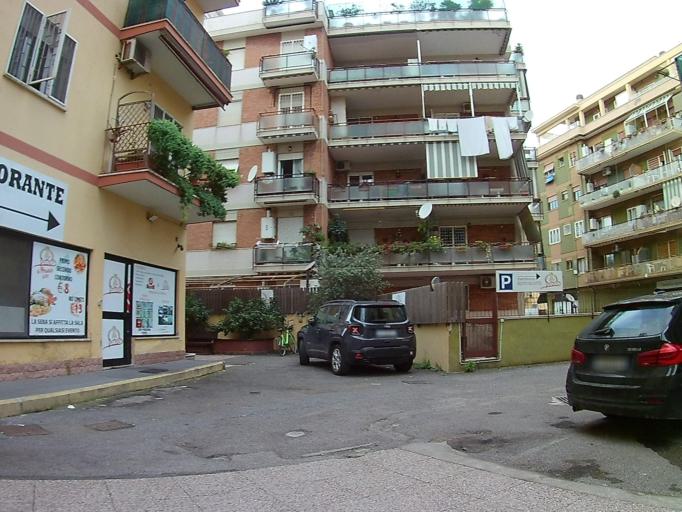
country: IT
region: Latium
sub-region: Citta metropolitana di Roma Capitale
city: Lido di Ostia
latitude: 41.7330
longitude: 12.2857
